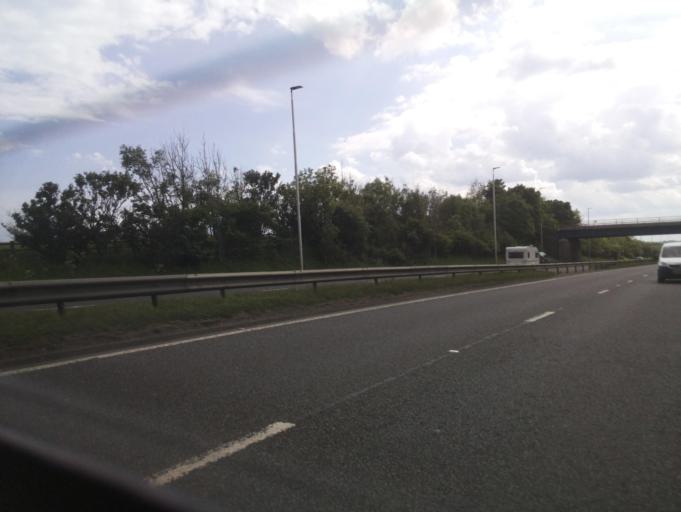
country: GB
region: England
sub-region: County Durham
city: Hawthorn
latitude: 54.8020
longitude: -1.3606
